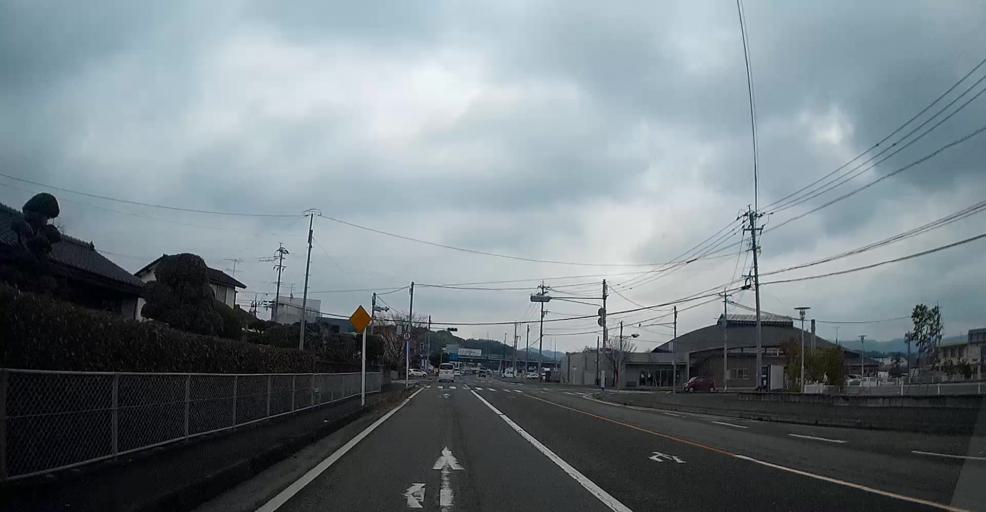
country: JP
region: Kumamoto
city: Matsubase
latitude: 32.6516
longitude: 130.6969
